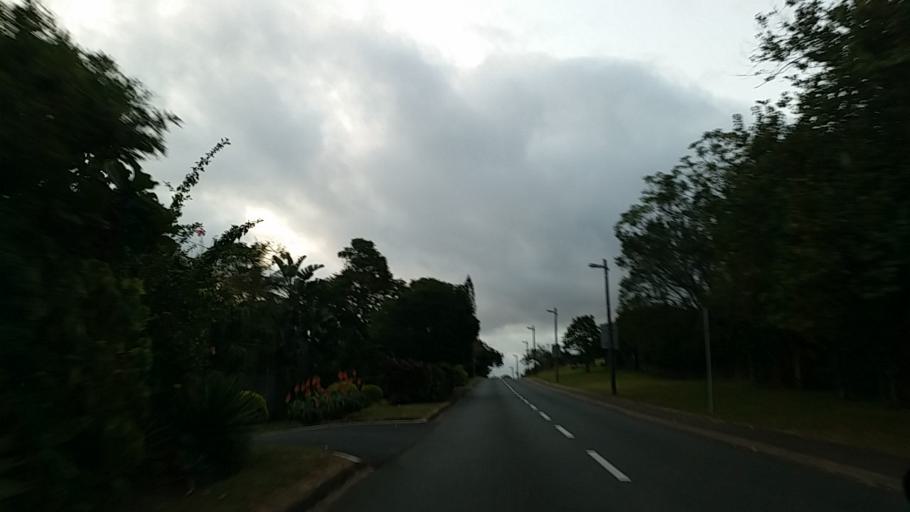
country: ZA
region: KwaZulu-Natal
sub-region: eThekwini Metropolitan Municipality
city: Berea
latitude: -29.8518
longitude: 30.9081
